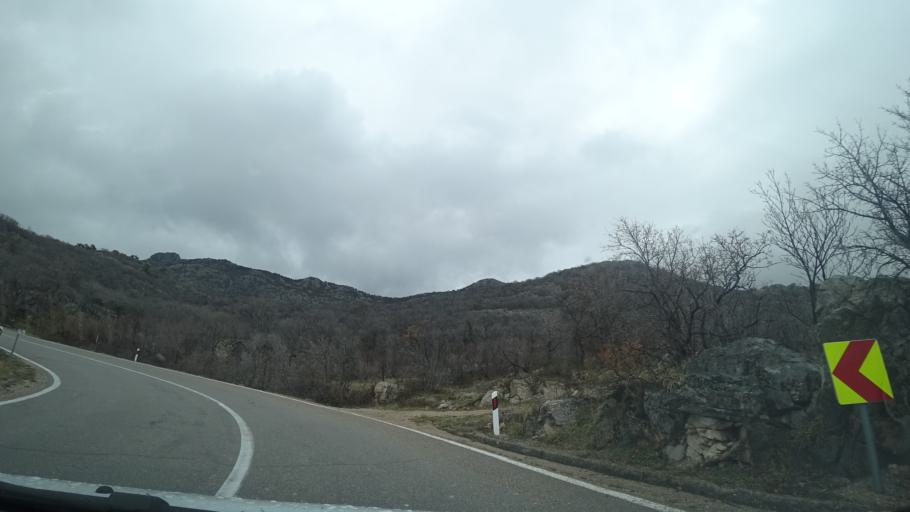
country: HR
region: Licko-Senjska
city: Karlobag
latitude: 44.5102
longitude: 15.1229
